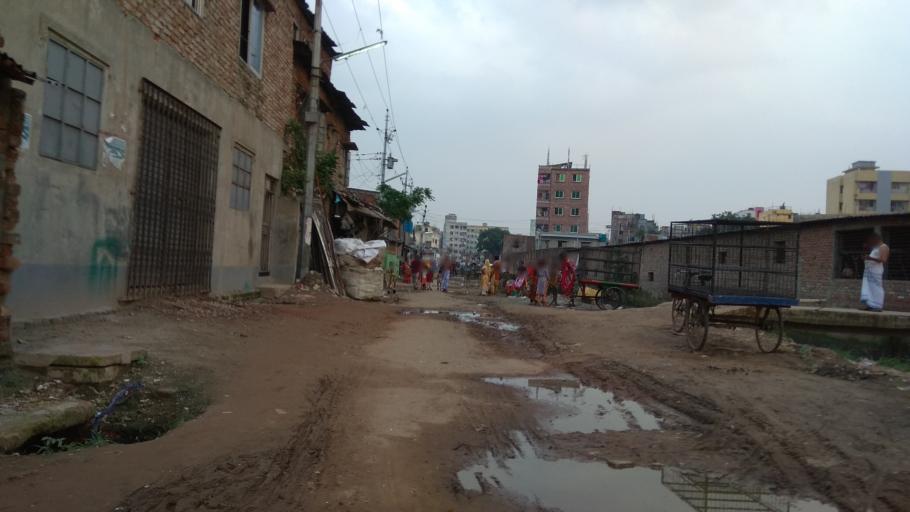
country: BD
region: Dhaka
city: Tungi
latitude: 23.8194
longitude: 90.3753
